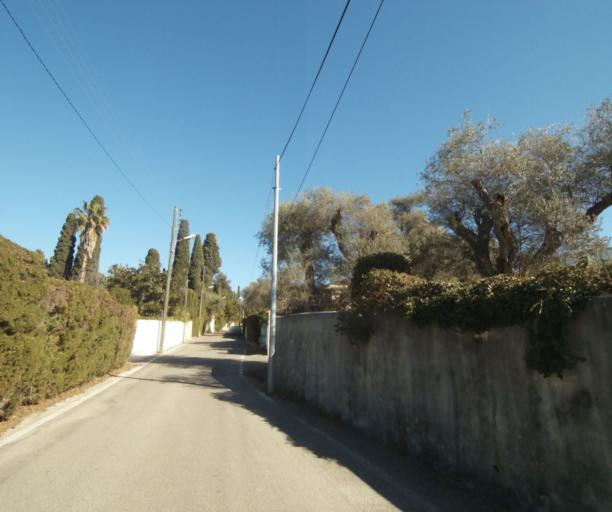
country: FR
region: Provence-Alpes-Cote d'Azur
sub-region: Departement des Alpes-Maritimes
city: Antibes
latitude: 43.5584
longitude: 7.1245
